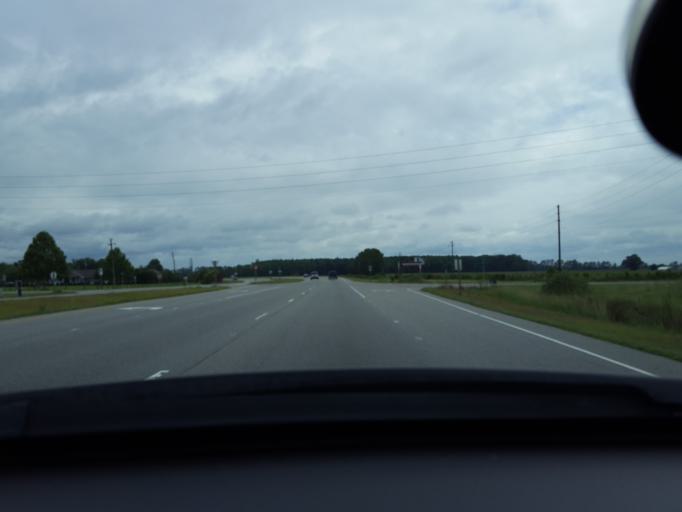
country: US
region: North Carolina
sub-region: Pitt County
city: Ayden
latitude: 35.4674
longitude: -77.4359
